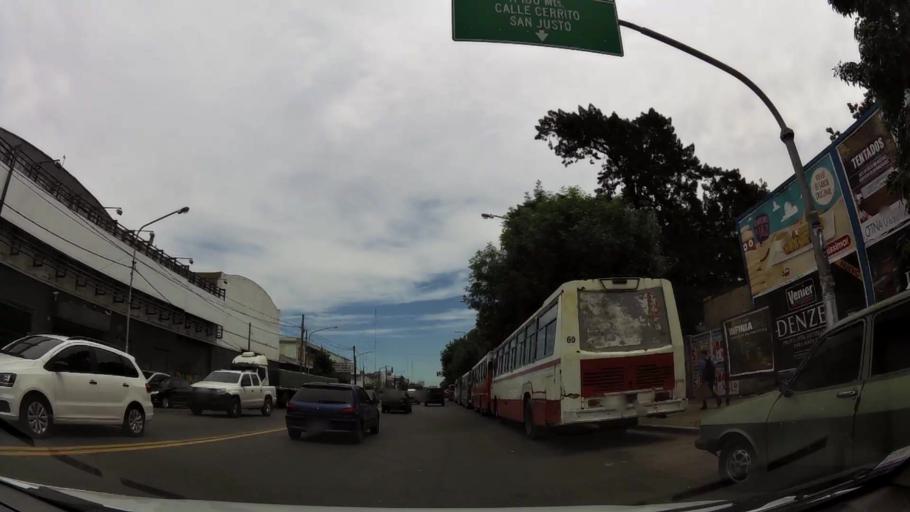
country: AR
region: Buenos Aires
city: San Justo
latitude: -34.6689
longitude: -58.5343
